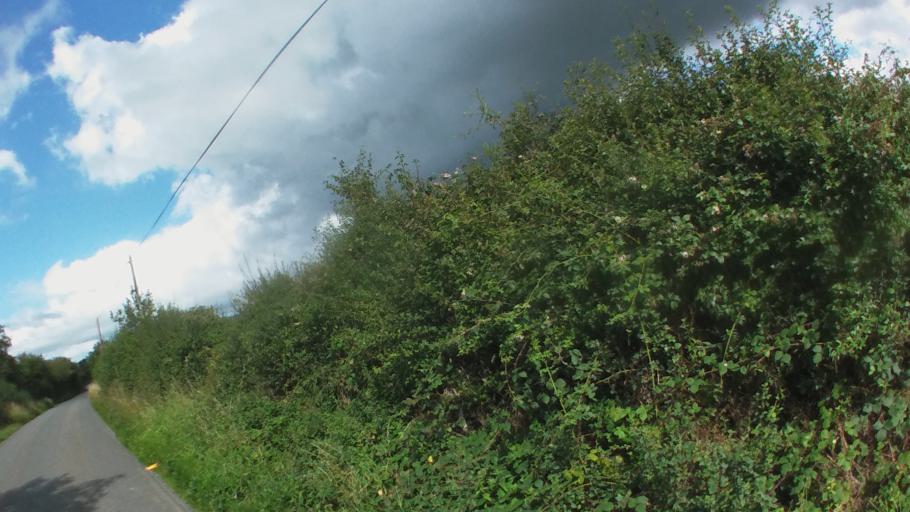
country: IE
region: Leinster
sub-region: Kilkenny
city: Kilkenny
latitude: 52.6817
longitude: -7.2210
